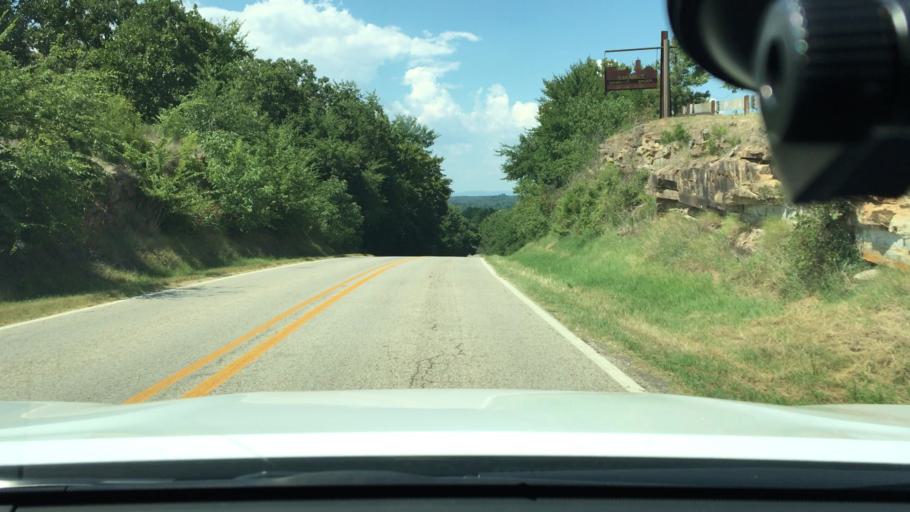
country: US
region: Arkansas
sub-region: Logan County
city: Paris
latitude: 35.3126
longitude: -93.6327
